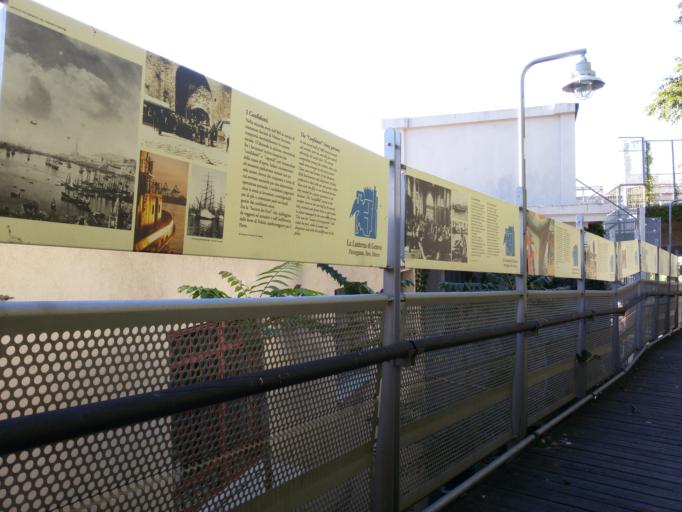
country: IT
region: Liguria
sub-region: Provincia di Genova
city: San Teodoro
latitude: 44.4068
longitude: 8.9070
